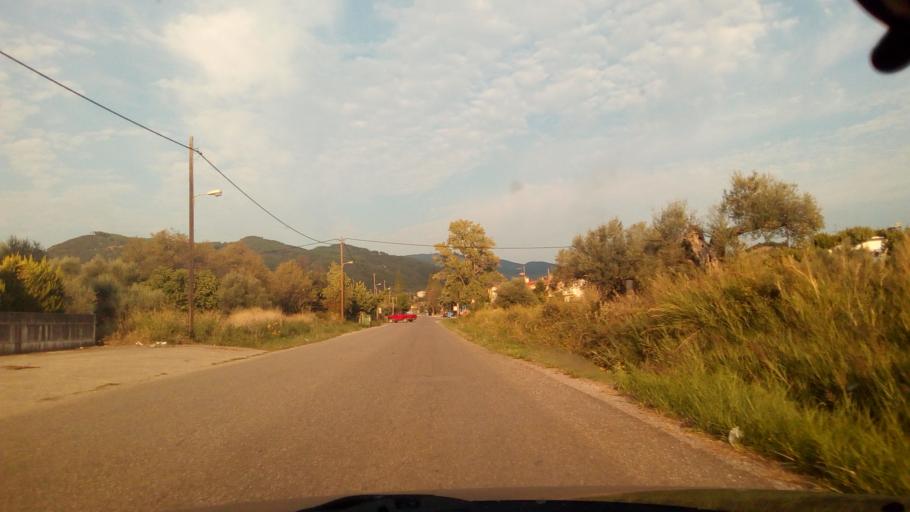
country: GR
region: West Greece
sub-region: Nomos Aitolias kai Akarnanias
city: Nafpaktos
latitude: 38.3964
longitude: 21.8029
